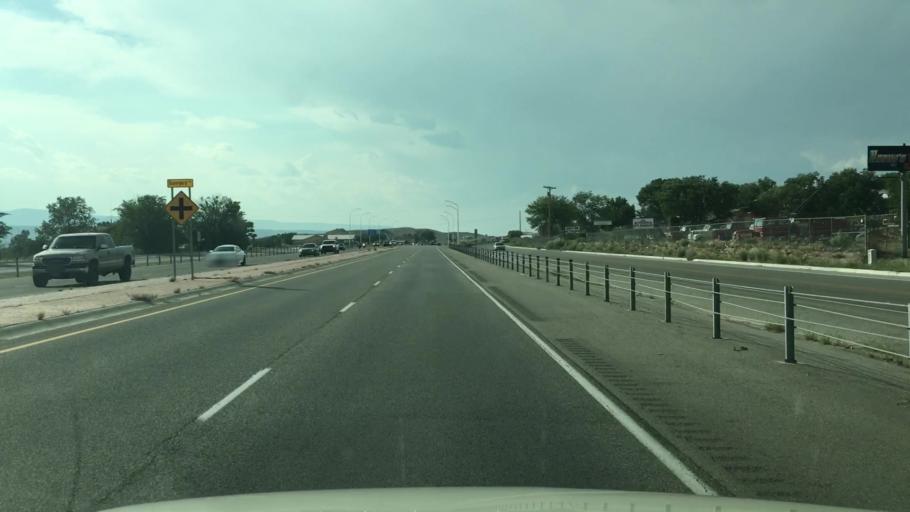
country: US
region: New Mexico
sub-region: Santa Fe County
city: El Valle de Arroyo Seco
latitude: 35.9669
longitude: -106.0348
